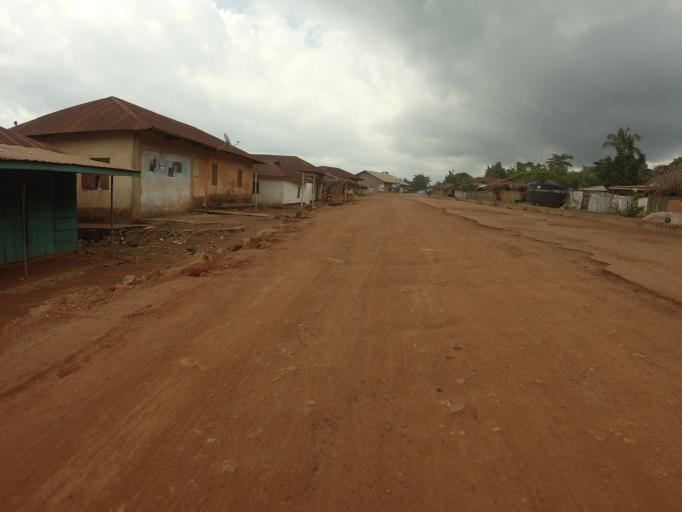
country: TG
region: Plateaux
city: Kpalime
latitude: 6.9193
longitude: 0.4604
